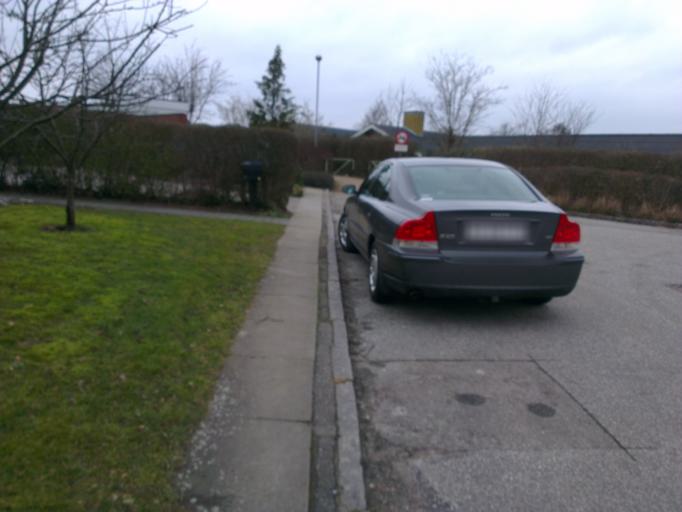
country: DK
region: Capital Region
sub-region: Frederikssund Kommune
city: Frederikssund
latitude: 55.8464
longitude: 12.0519
